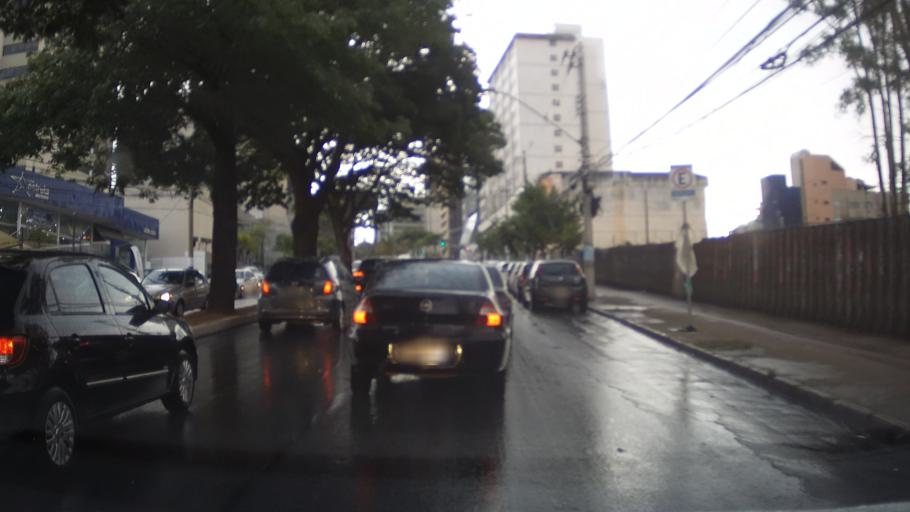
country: BR
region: Minas Gerais
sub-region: Belo Horizonte
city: Belo Horizonte
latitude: -19.9457
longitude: -43.9580
